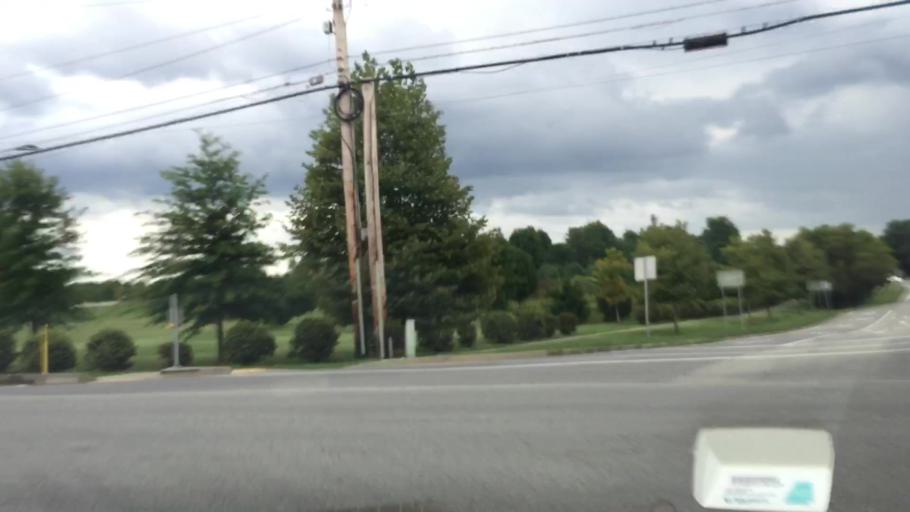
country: US
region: Pennsylvania
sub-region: Butler County
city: Cranberry Township
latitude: 40.6987
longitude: -80.1137
